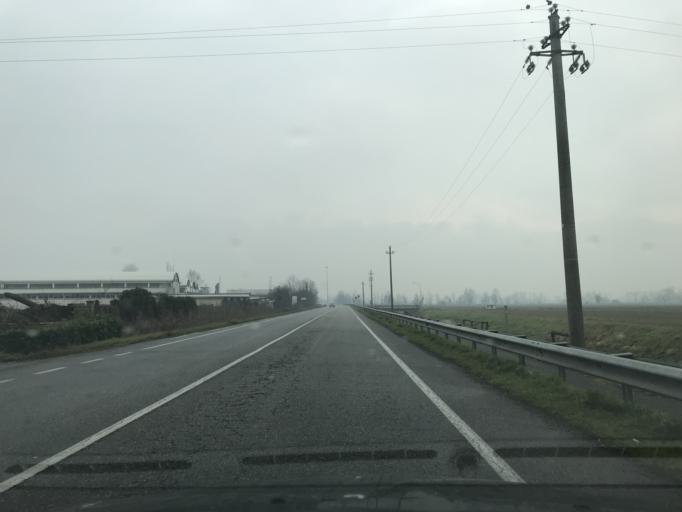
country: IT
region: Lombardy
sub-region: Provincia di Lodi
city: Lodi
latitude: 45.2898
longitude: 9.5043
